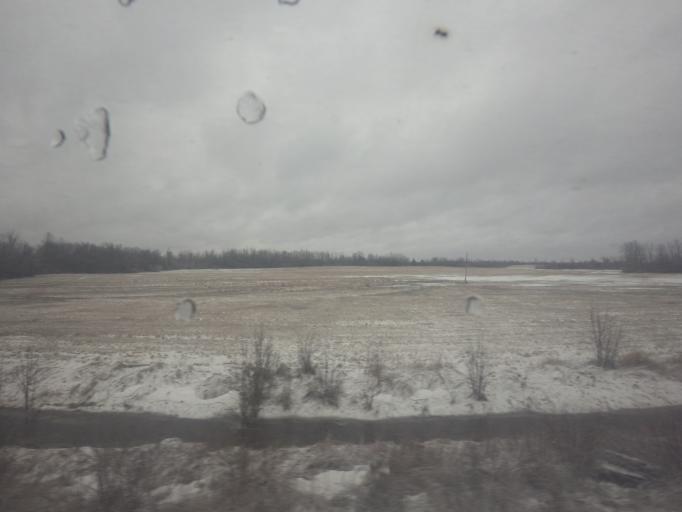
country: CA
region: Ontario
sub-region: Lanark County
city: Smiths Falls
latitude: 44.9254
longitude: -76.0262
